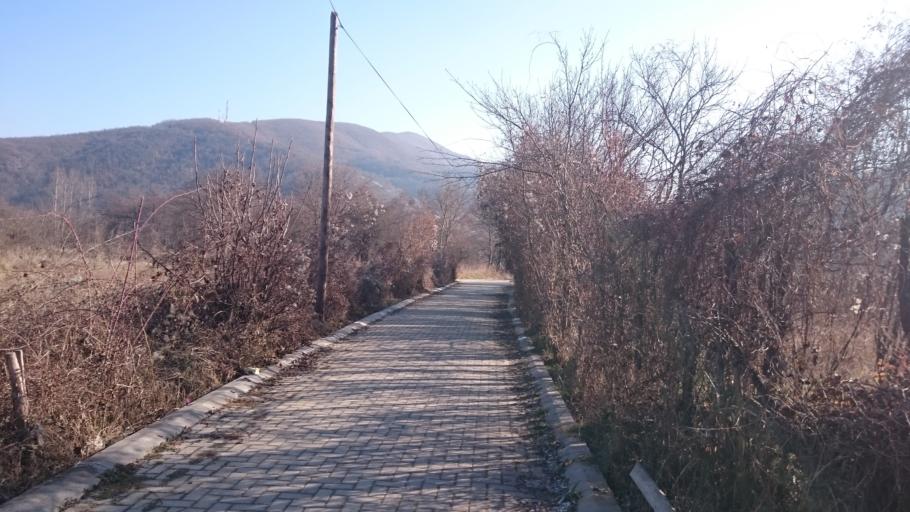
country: MK
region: Makedonski Brod
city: Makedonski Brod
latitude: 41.5111
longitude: 21.2190
